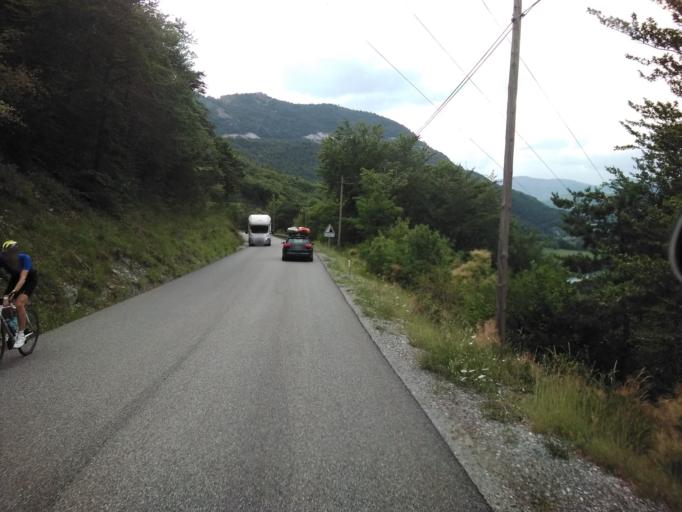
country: FR
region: Provence-Alpes-Cote d'Azur
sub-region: Departement des Alpes-de-Haute-Provence
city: Seyne-les-Alpes
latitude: 44.4490
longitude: 6.4015
